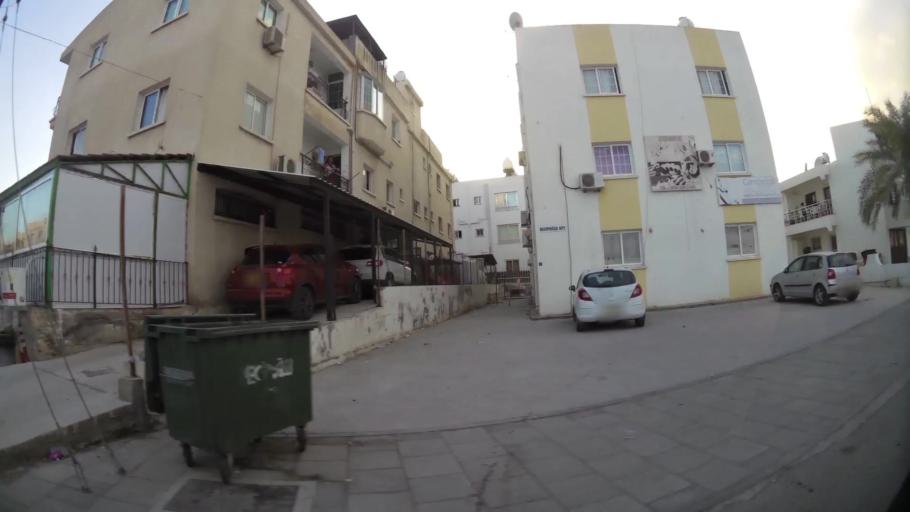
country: CY
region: Lefkosia
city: Nicosia
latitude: 35.2006
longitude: 33.3729
